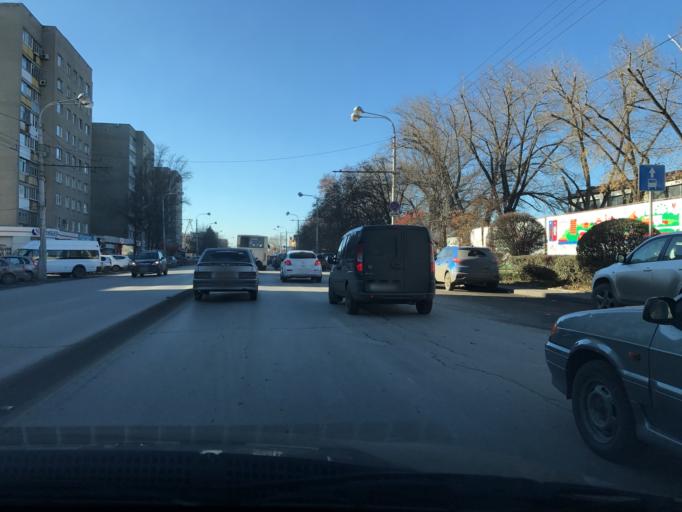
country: RU
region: Rostov
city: Rostov-na-Donu
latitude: 47.2111
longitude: 39.6701
